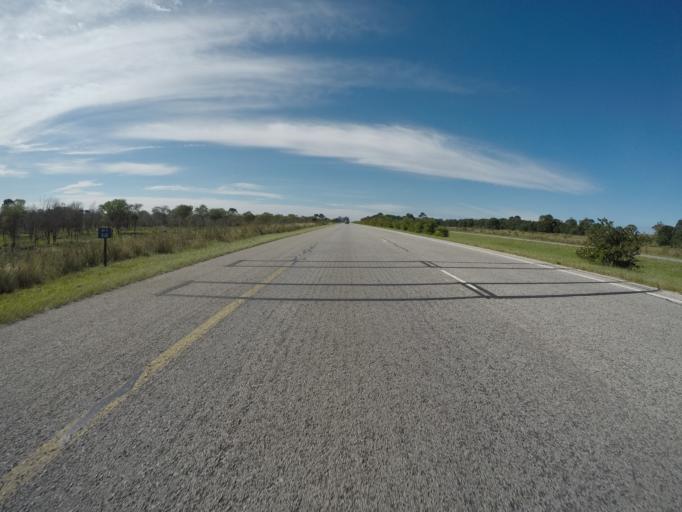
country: ZA
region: Eastern Cape
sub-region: Nelson Mandela Bay Metropolitan Municipality
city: Uitenhage
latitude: -33.9331
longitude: 25.3546
